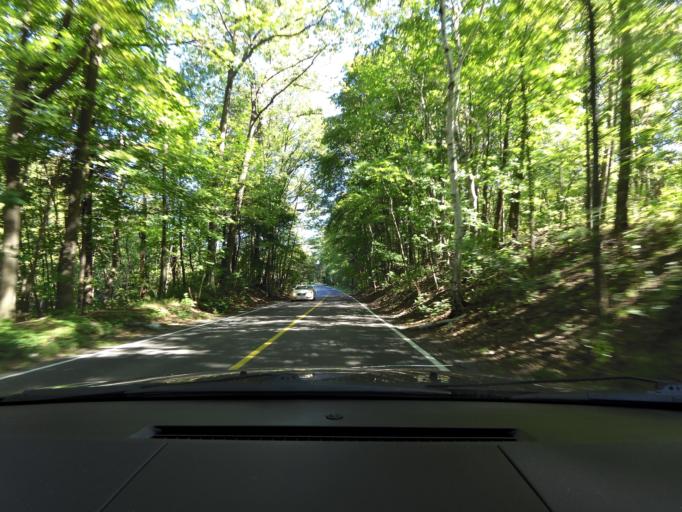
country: CA
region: Ontario
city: Hamilton
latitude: 43.3044
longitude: -79.8427
